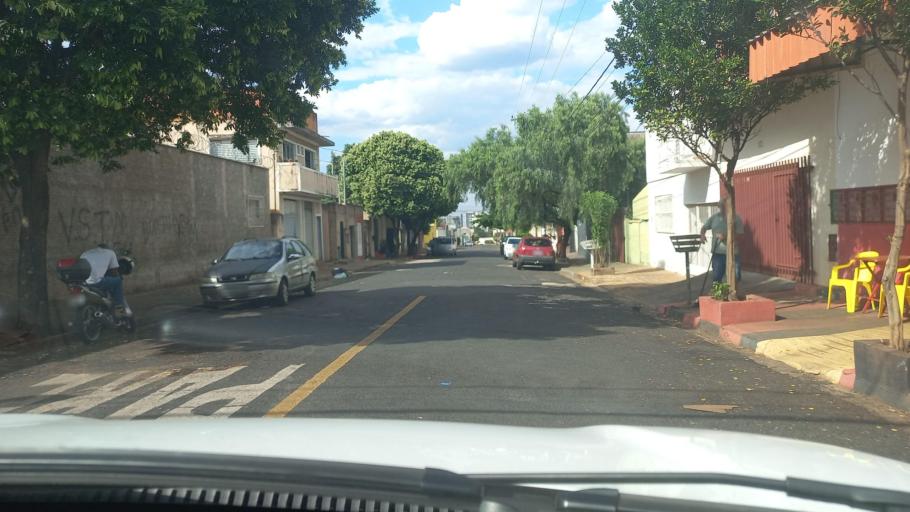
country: BR
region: Minas Gerais
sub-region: Uberaba
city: Uberaba
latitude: -19.7632
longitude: -47.9527
